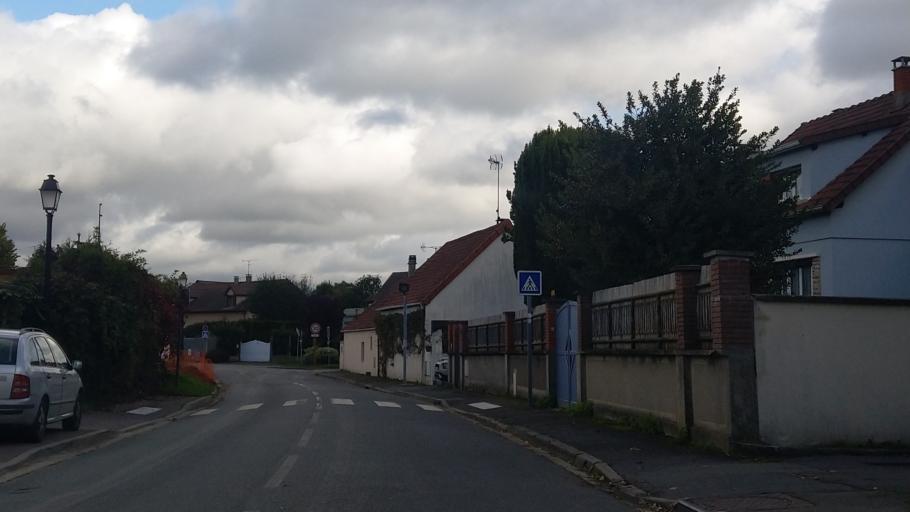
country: FR
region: Ile-de-France
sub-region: Departement du Val-d'Oise
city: Baillet-en-France
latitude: 49.0580
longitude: 2.2945
